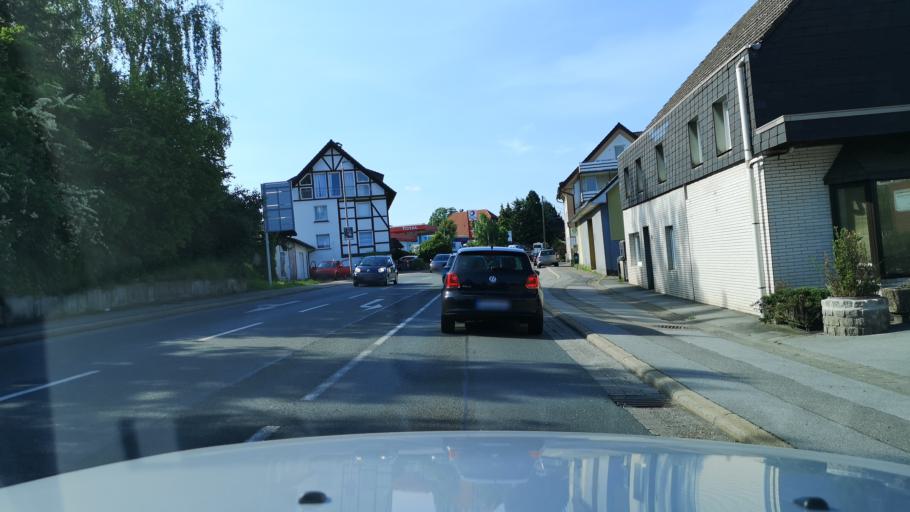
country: DE
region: North Rhine-Westphalia
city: Iserlohn
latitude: 51.4251
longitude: 7.6765
